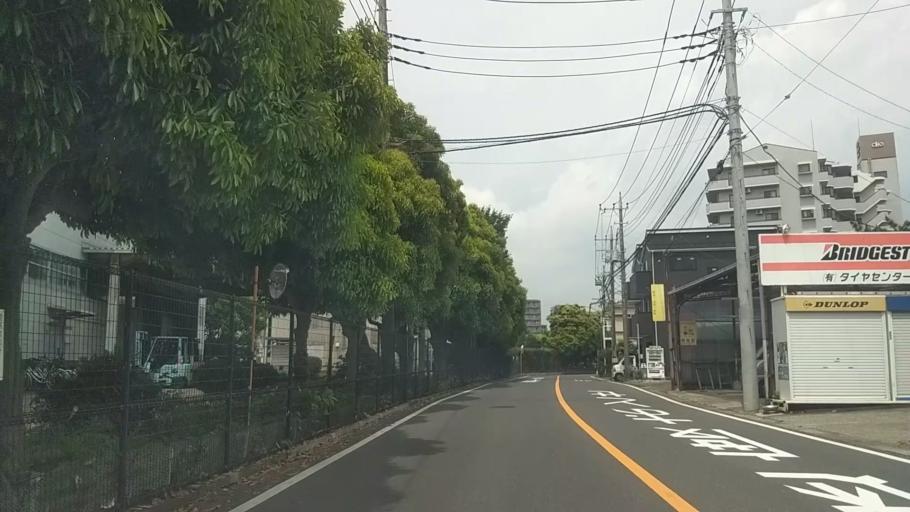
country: JP
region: Kanagawa
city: Fujisawa
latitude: 35.3599
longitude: 139.4660
